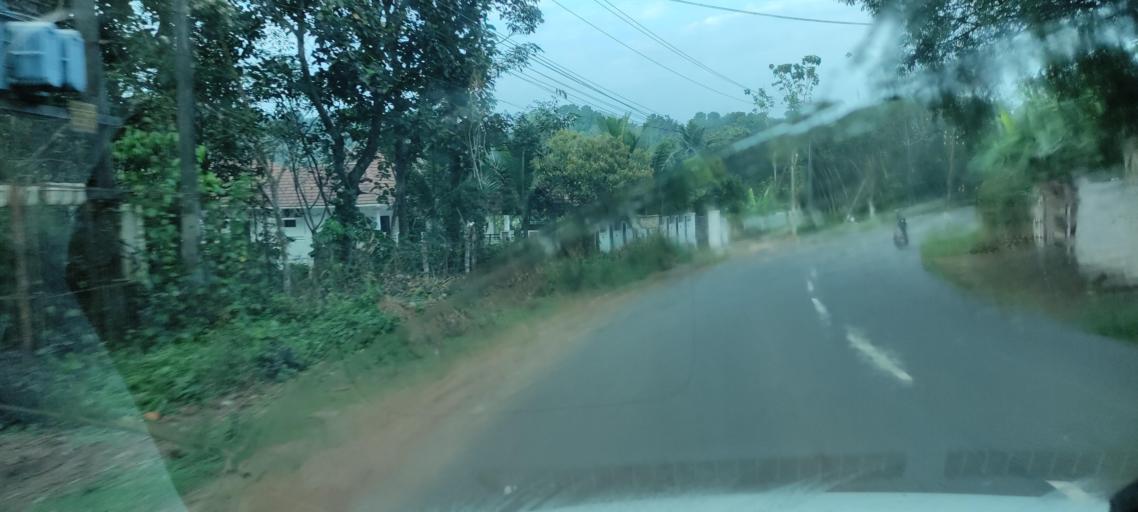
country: IN
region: Kerala
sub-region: Pattanamtitta
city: Adur
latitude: 9.1256
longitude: 76.7030
